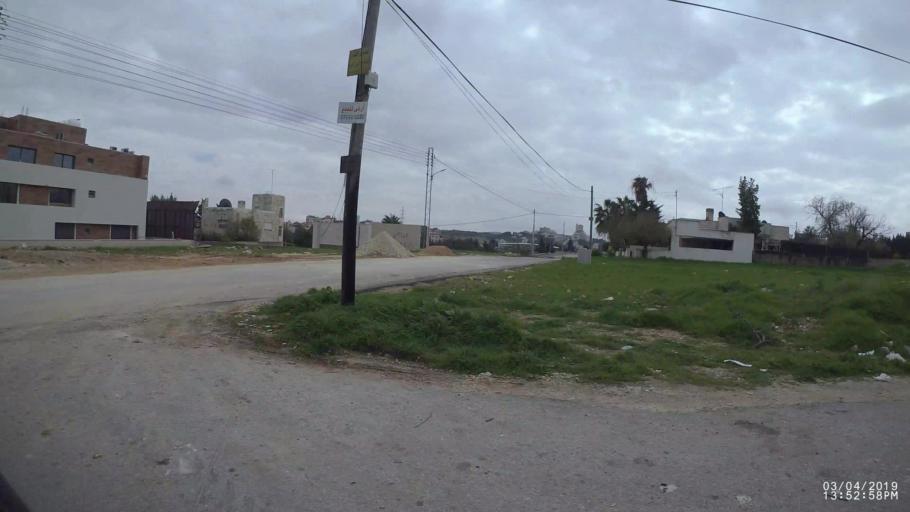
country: JO
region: Amman
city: Umm as Summaq
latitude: 31.9264
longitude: 35.8585
